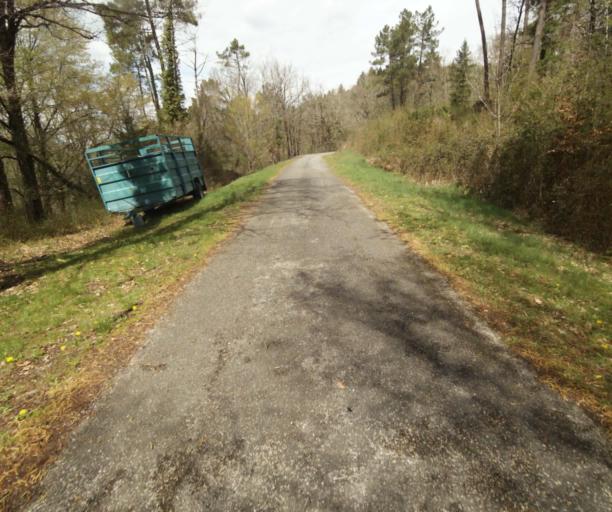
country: FR
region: Limousin
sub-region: Departement de la Correze
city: Sainte-Fortunade
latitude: 45.1791
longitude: 1.8706
